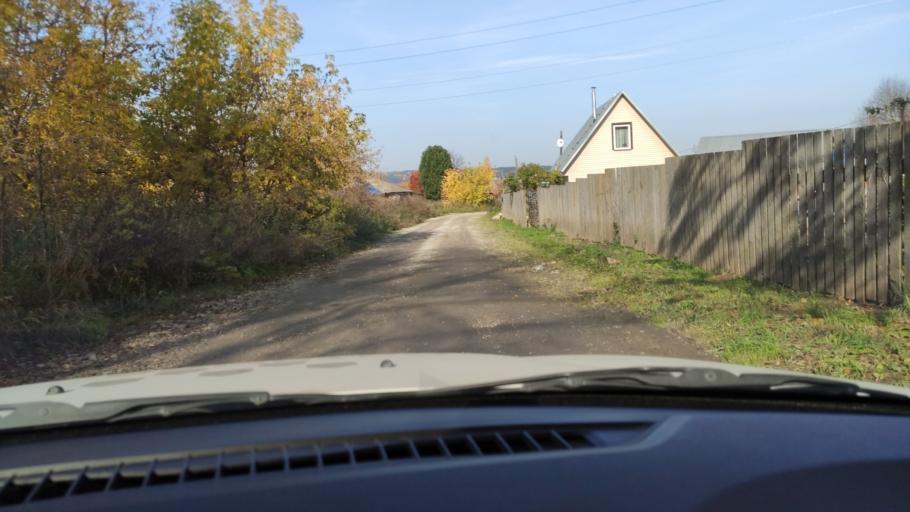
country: RU
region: Perm
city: Sylva
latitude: 58.0453
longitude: 56.7382
